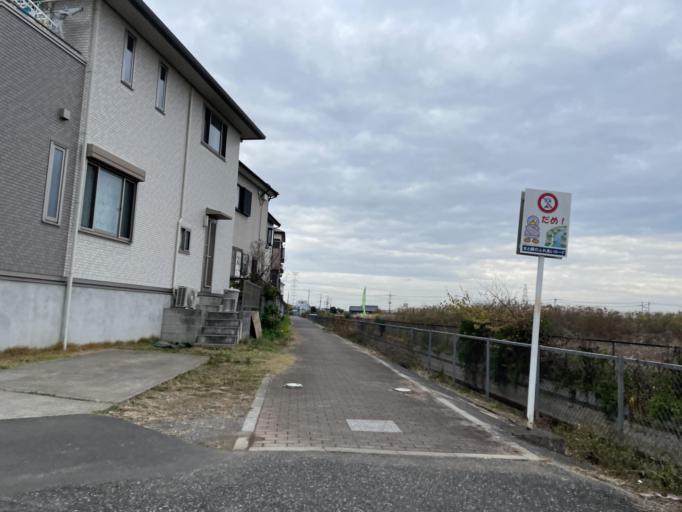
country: JP
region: Saitama
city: Shiraoka
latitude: 36.0301
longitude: 139.6587
